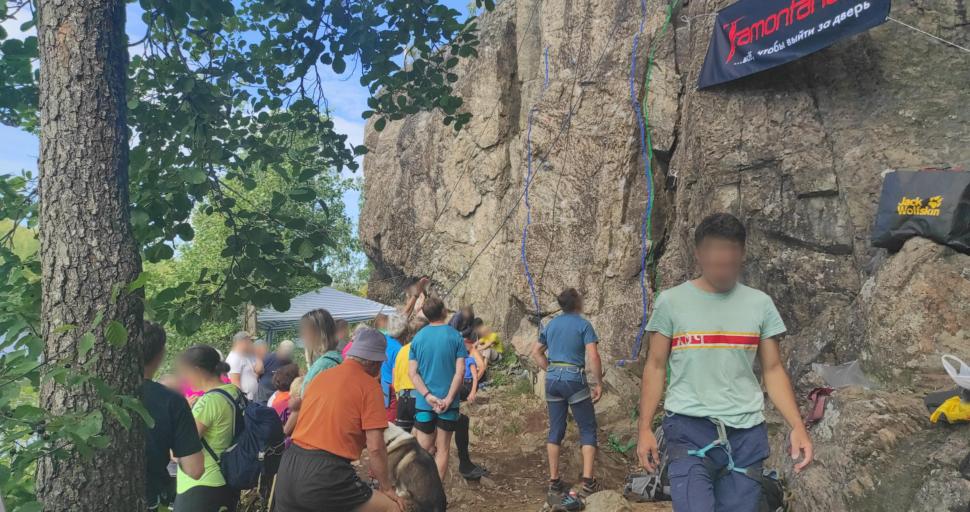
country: RU
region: Leningrad
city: Kuznechnoye
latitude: 61.1640
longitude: 29.7019
